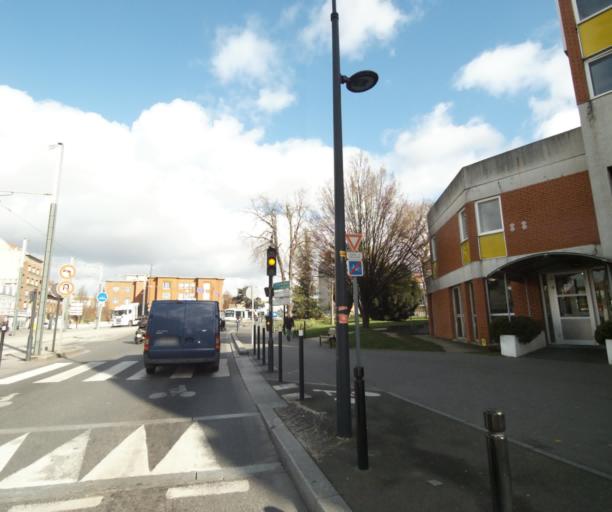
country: FR
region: Ile-de-France
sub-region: Departement de Seine-Saint-Denis
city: Pierrefitte-sur-Seine
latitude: 48.9628
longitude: 2.3594
